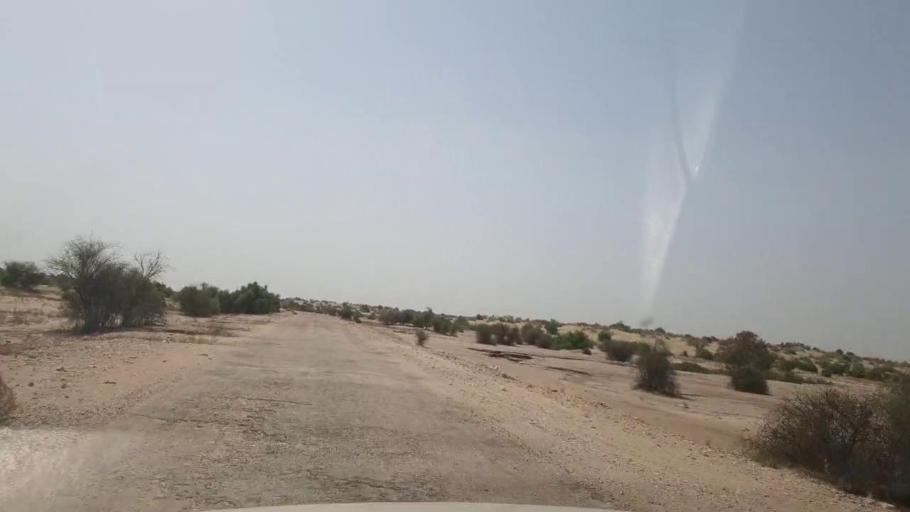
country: PK
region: Sindh
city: Rohri
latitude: 27.4383
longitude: 69.2441
